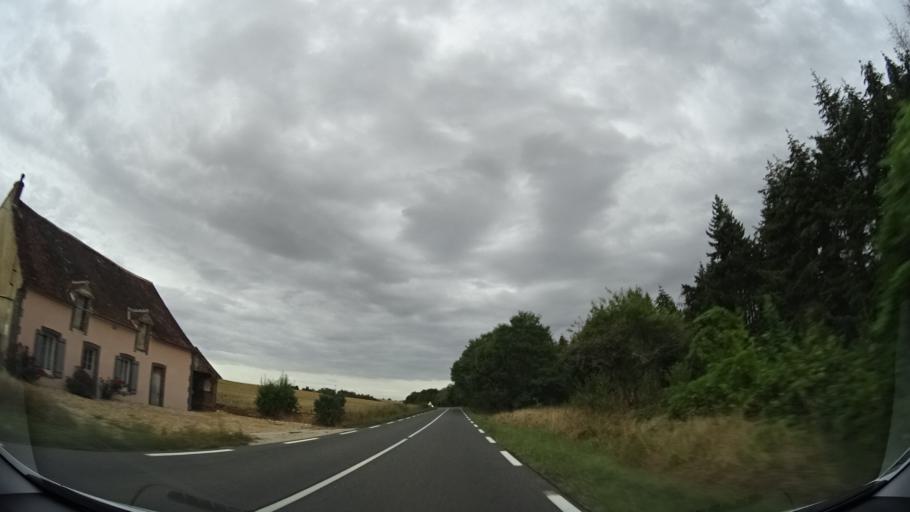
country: FR
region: Centre
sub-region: Departement du Loiret
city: Saint-Germain-des-Pres
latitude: 47.9477
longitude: 2.8640
